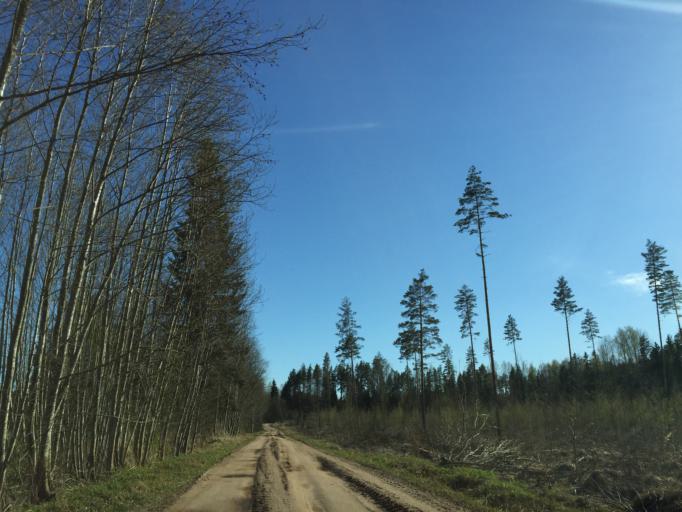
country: EE
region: Valgamaa
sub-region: Valga linn
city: Valga
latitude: 57.7794
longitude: 26.2329
